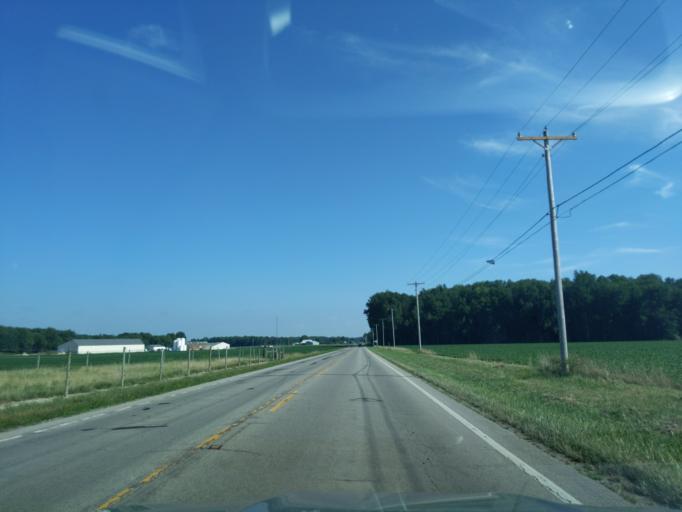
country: US
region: Indiana
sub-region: Ripley County
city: Osgood
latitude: 39.1743
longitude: -85.3143
